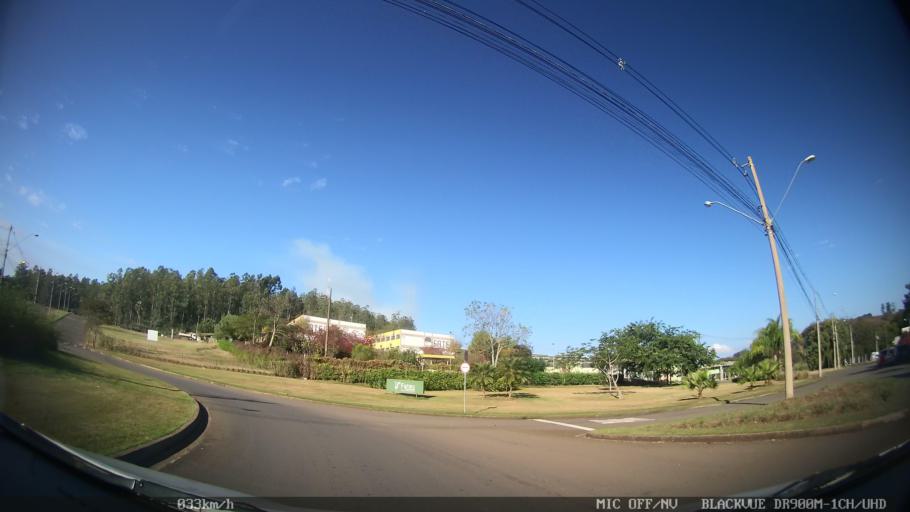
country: BR
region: Sao Paulo
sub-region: Piracicaba
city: Piracicaba
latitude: -22.6926
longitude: -47.6262
